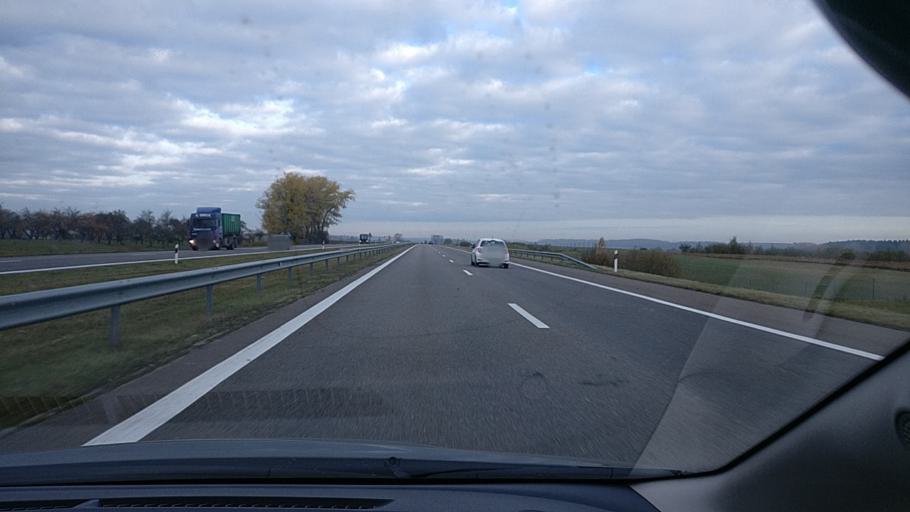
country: LT
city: Sirvintos
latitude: 55.1241
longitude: 24.8409
